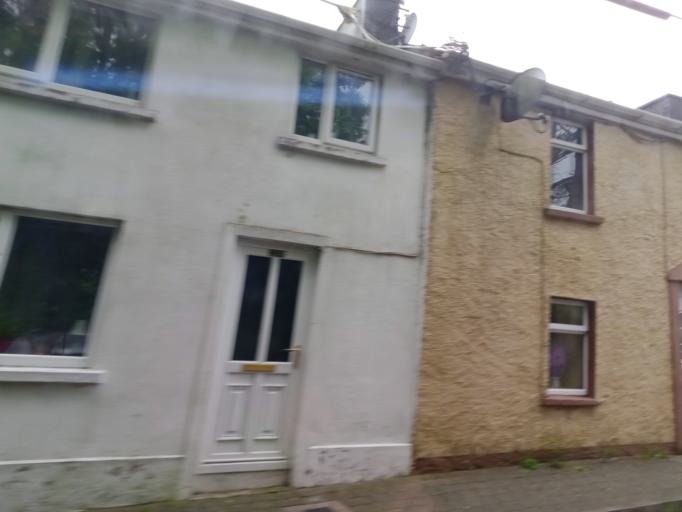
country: IE
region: Munster
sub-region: County Cork
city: Bandon
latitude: 51.7440
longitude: -8.7290
